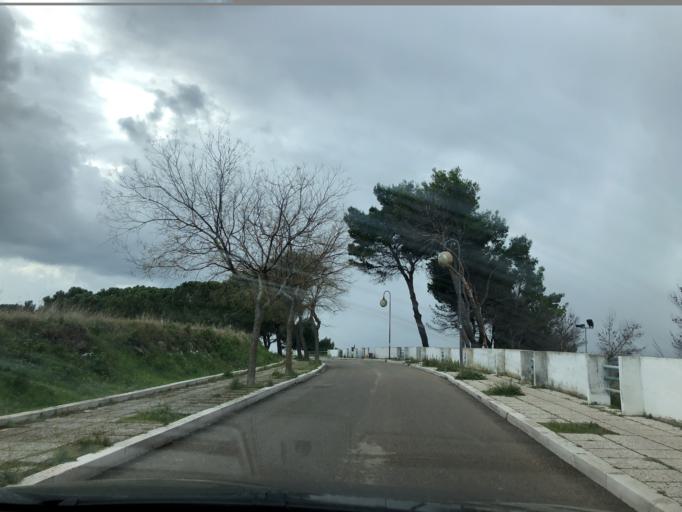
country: IT
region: Apulia
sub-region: Provincia di Foggia
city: Lucera
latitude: 41.5087
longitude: 15.3233
